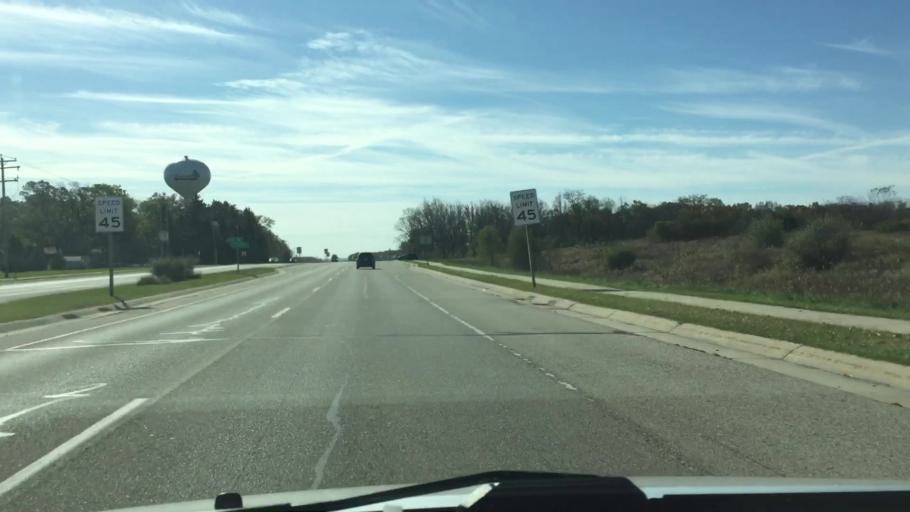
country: US
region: Wisconsin
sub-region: Waukesha County
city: Sussex
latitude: 43.1224
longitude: -88.2445
